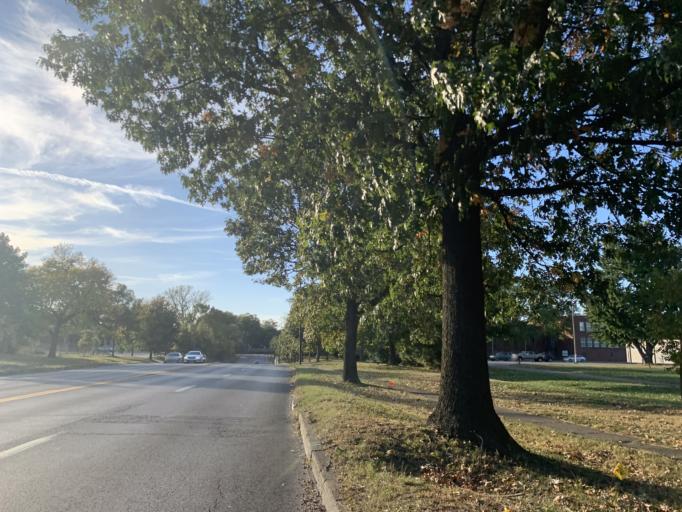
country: US
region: Kentucky
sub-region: Jefferson County
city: Louisville
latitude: 38.2212
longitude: -85.7790
